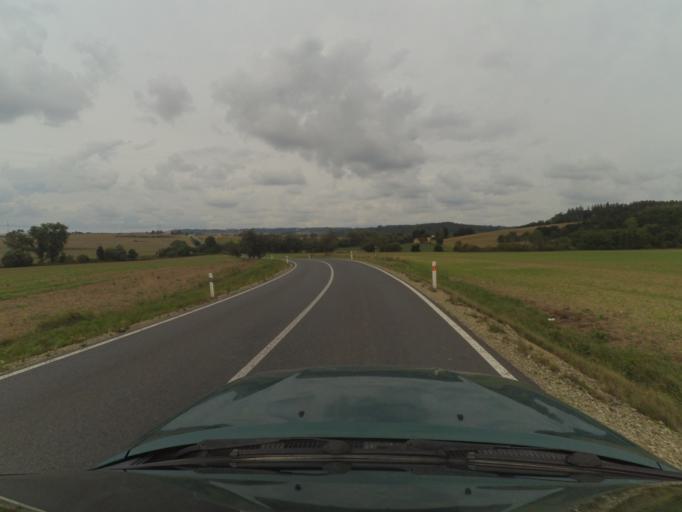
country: CZ
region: Central Bohemia
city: Luzna
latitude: 50.1628
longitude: 13.7441
